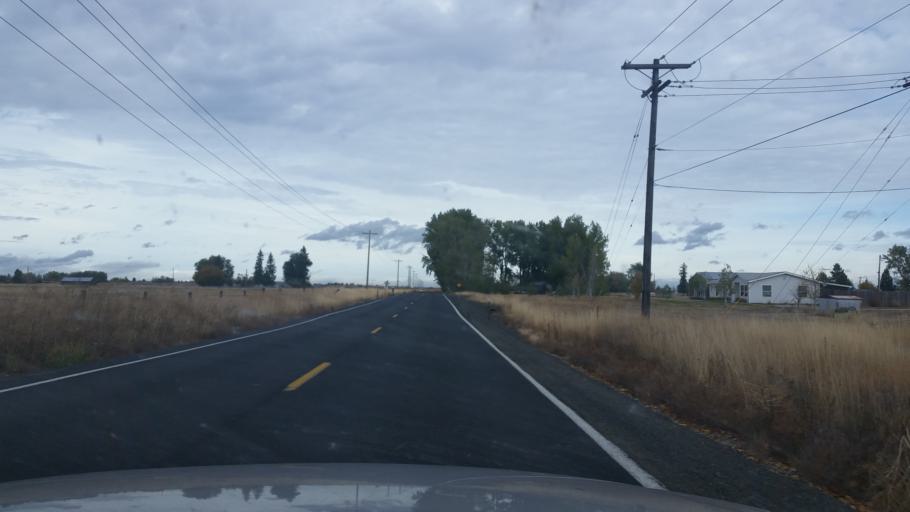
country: US
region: Washington
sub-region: Spokane County
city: Airway Heights
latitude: 47.6108
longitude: -117.6075
